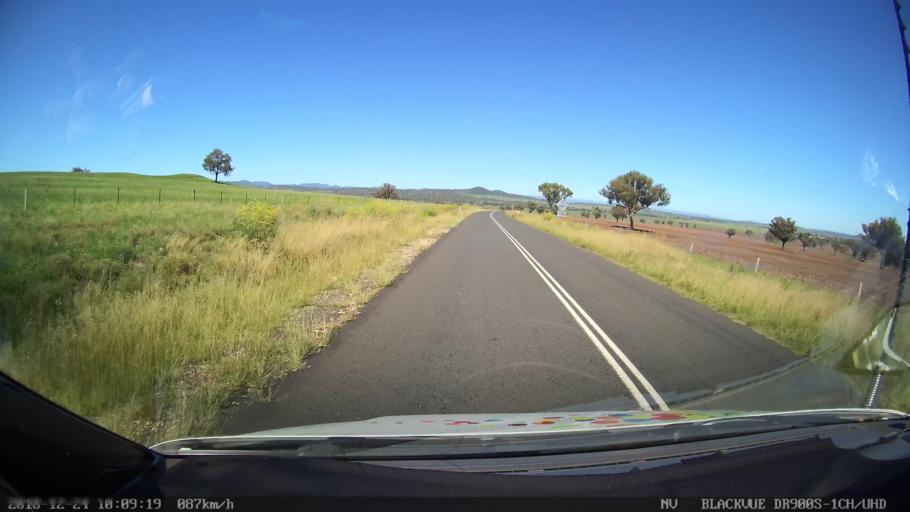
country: AU
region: New South Wales
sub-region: Liverpool Plains
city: Quirindi
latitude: -31.6626
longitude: 150.6927
